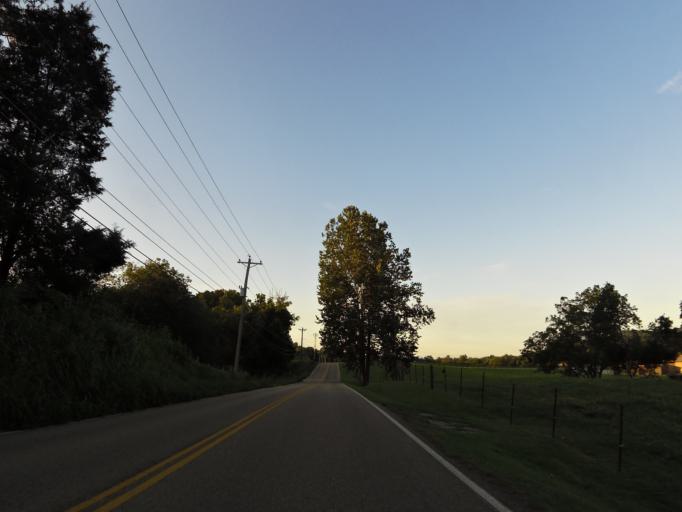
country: US
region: Tennessee
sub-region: Roane County
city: Midtown
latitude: 35.7818
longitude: -84.5802
